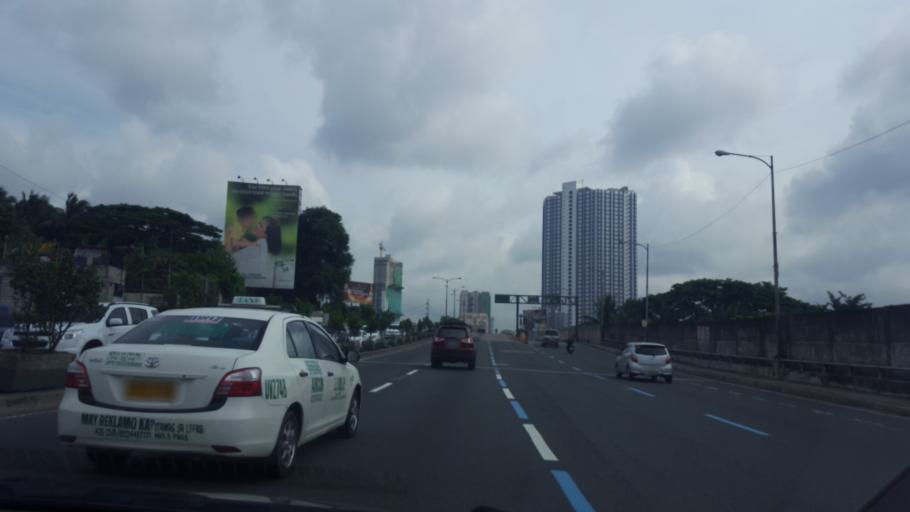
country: PH
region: Metro Manila
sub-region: Marikina
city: Calumpang
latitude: 14.6279
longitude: 121.0742
